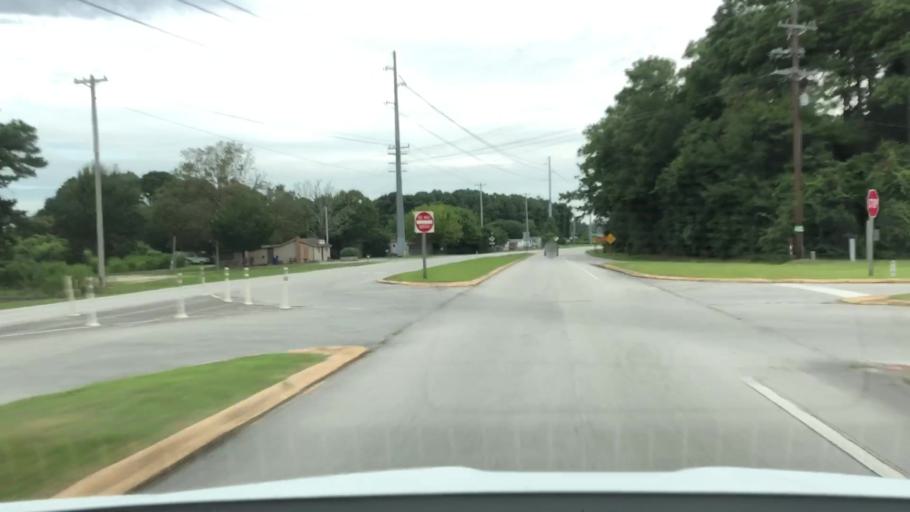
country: US
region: North Carolina
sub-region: Carteret County
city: Cape Carteret
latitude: 34.7064
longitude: -77.0682
